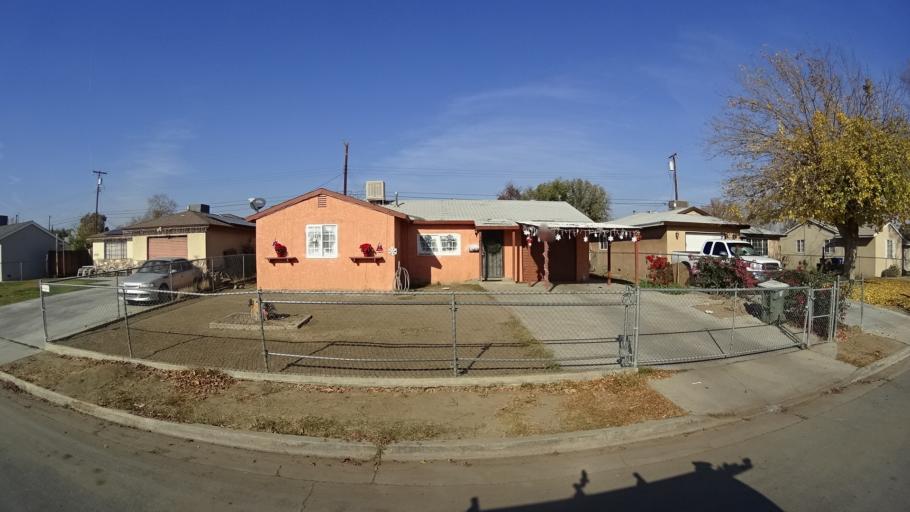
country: US
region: California
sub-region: Kern County
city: Bakersfield
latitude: 35.3258
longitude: -119.0144
